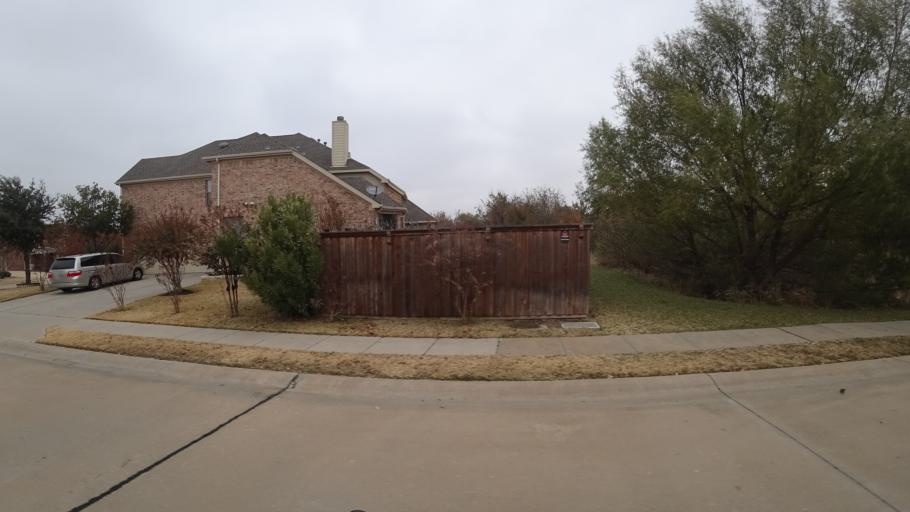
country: US
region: Texas
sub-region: Denton County
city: The Colony
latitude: 33.0700
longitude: -96.9070
